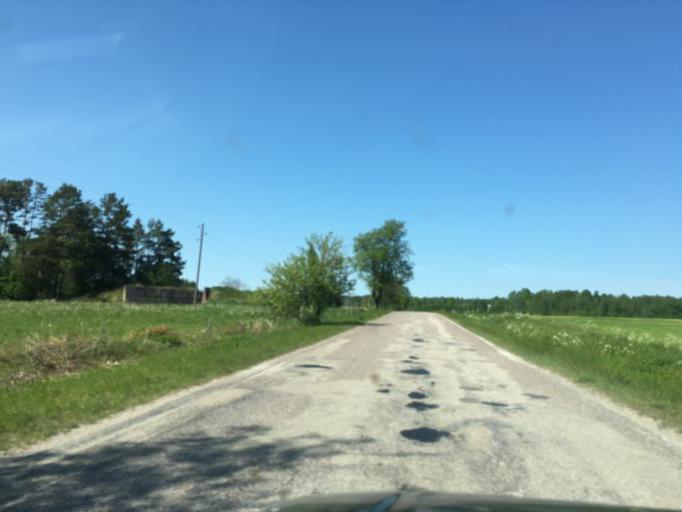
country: LV
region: Dundaga
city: Dundaga
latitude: 57.4636
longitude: 22.3224
